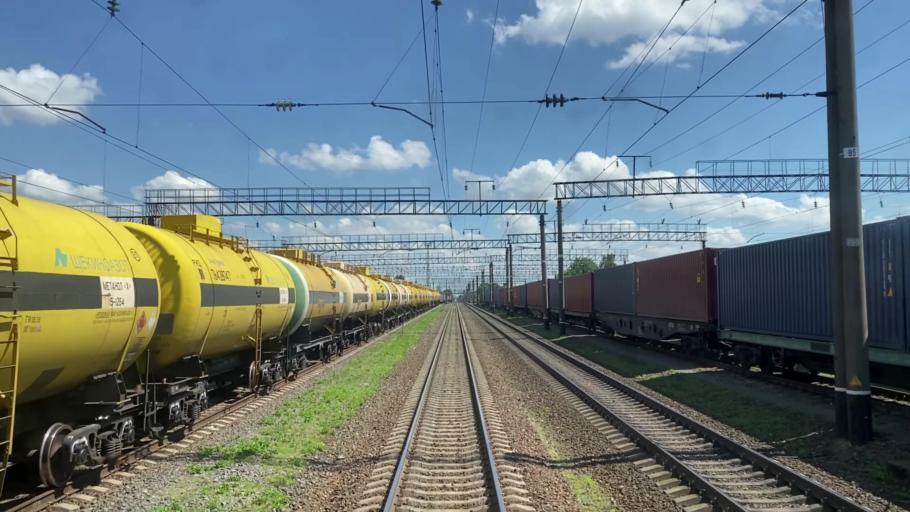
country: BY
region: Brest
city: Baranovichi
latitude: 53.1413
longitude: 26.0159
